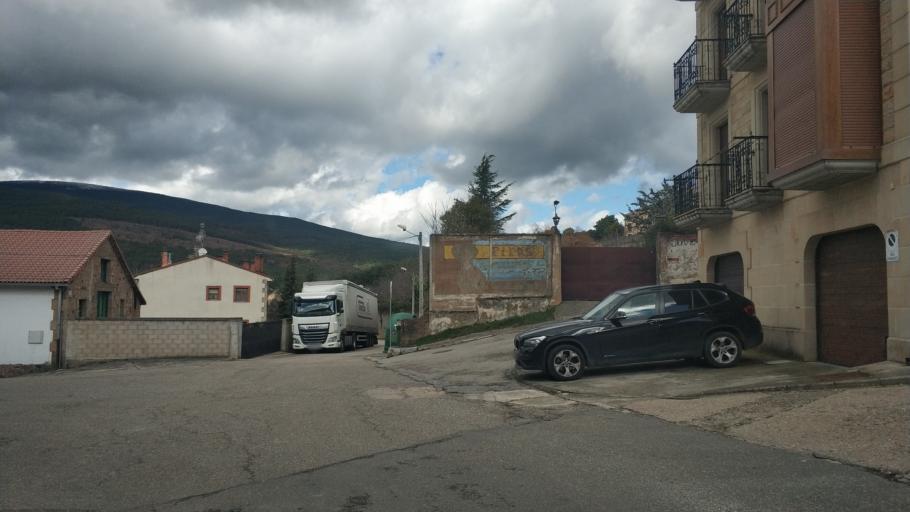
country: ES
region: Castille and Leon
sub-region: Provincia de Burgos
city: Quintanar de la Sierra
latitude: 41.9819
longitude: -3.0414
